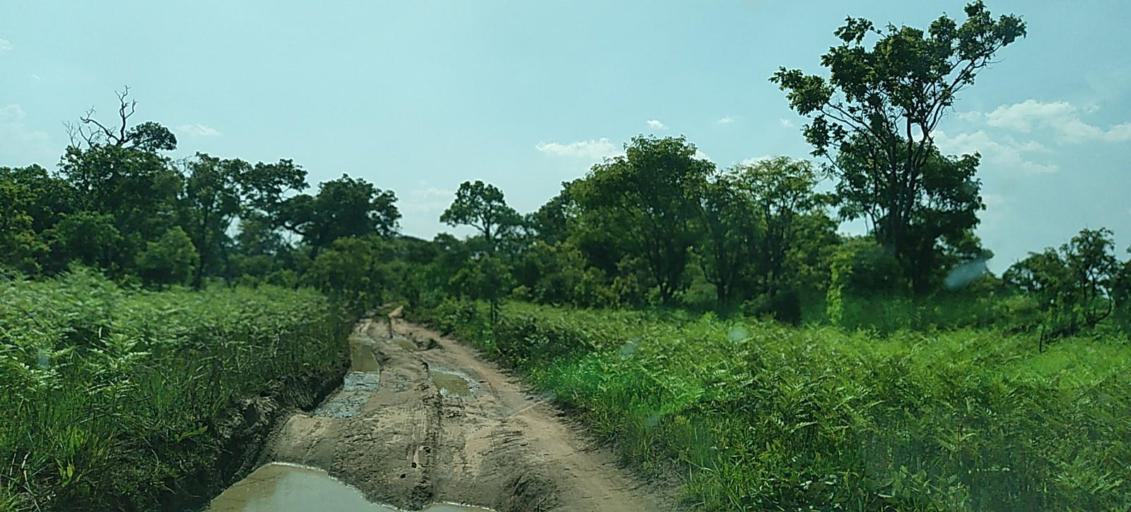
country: ZM
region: North-Western
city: Mwinilunga
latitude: -11.2733
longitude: 24.9841
